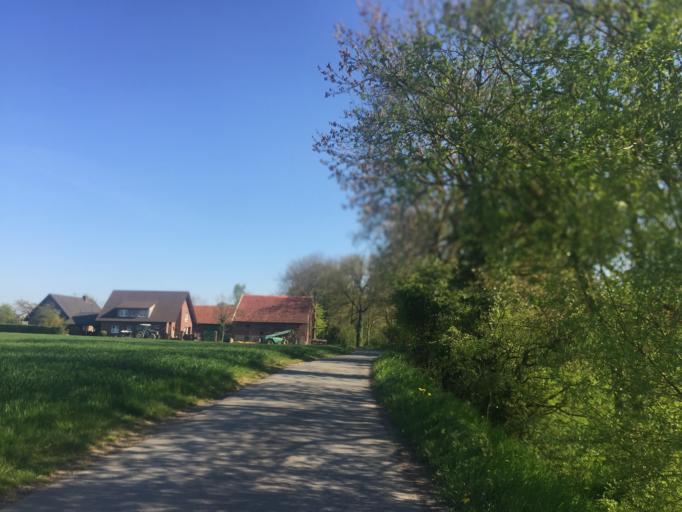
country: DE
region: North Rhine-Westphalia
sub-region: Regierungsbezirk Munster
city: Muenster
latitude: 51.9809
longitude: 7.5849
